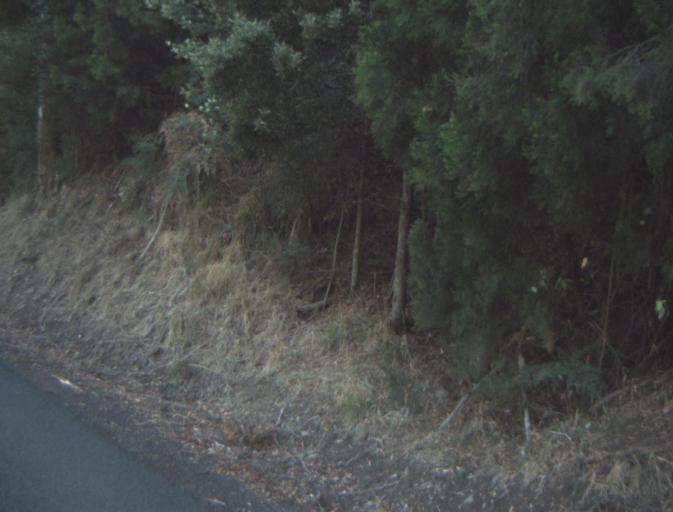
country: AU
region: Tasmania
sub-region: Launceston
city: Mayfield
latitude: -41.2962
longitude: 147.2014
